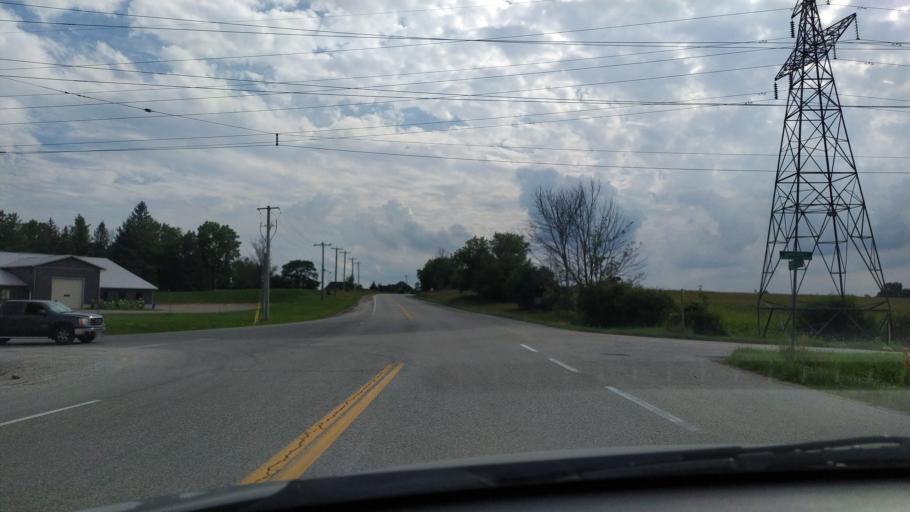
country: CA
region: Ontario
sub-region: Wellington County
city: Guelph
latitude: 43.4609
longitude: -80.1711
